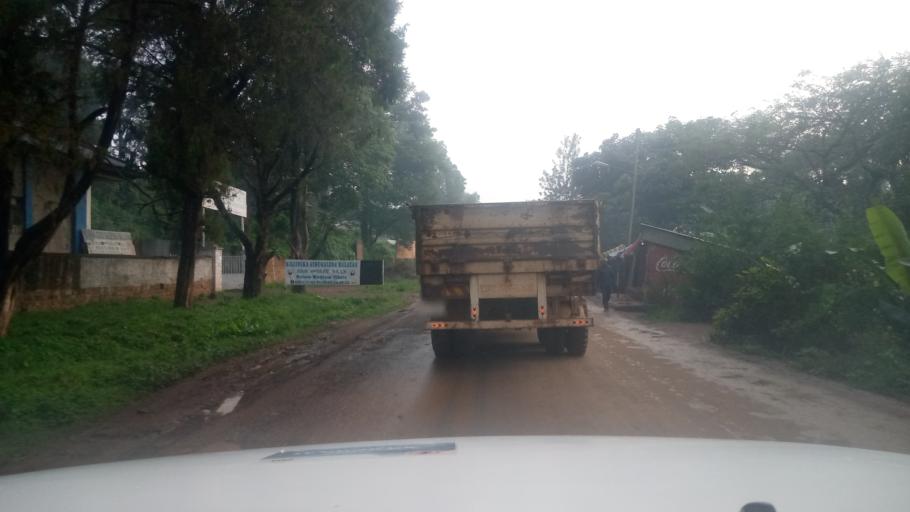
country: ET
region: Oromiya
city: Jima
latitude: 7.6781
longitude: 36.8344
